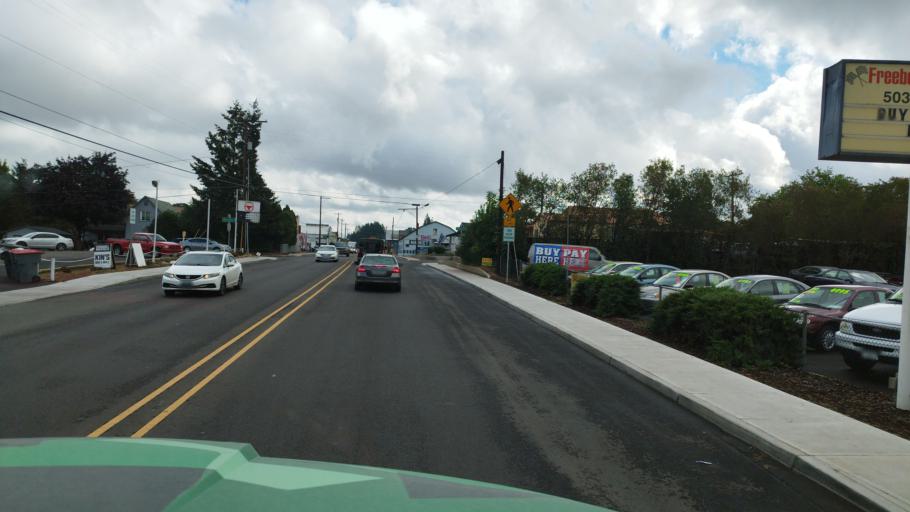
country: US
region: Oregon
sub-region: Yamhill County
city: Lafayette
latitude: 45.2449
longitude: -123.1186
